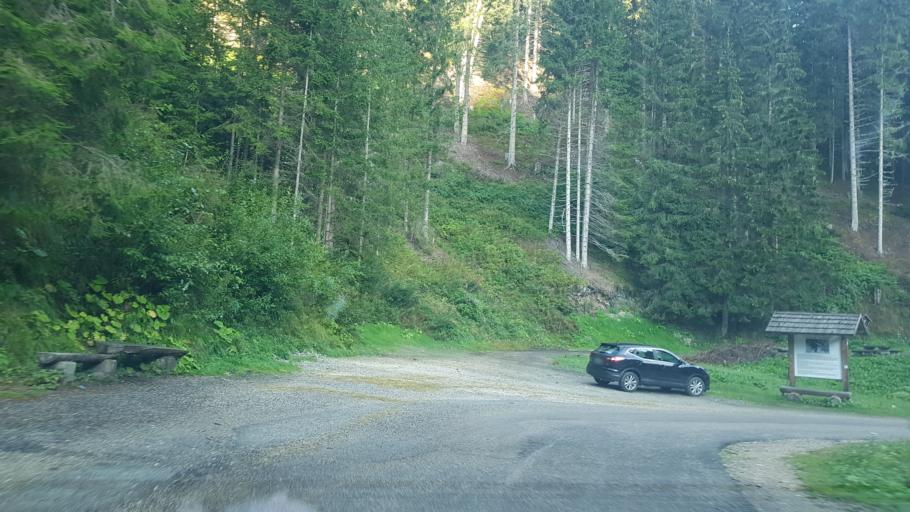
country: IT
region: Veneto
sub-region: Provincia di Belluno
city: San Pietro di Cadore
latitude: 46.5923
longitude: 12.5797
